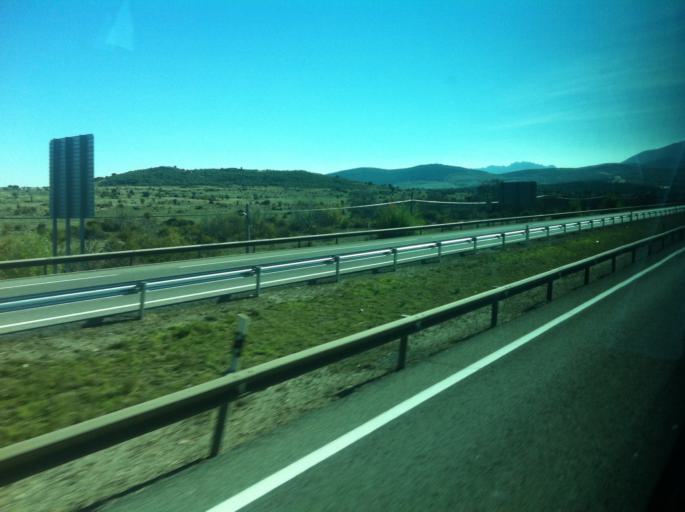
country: ES
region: Madrid
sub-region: Provincia de Madrid
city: Gascones
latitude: 41.0218
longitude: -3.6257
